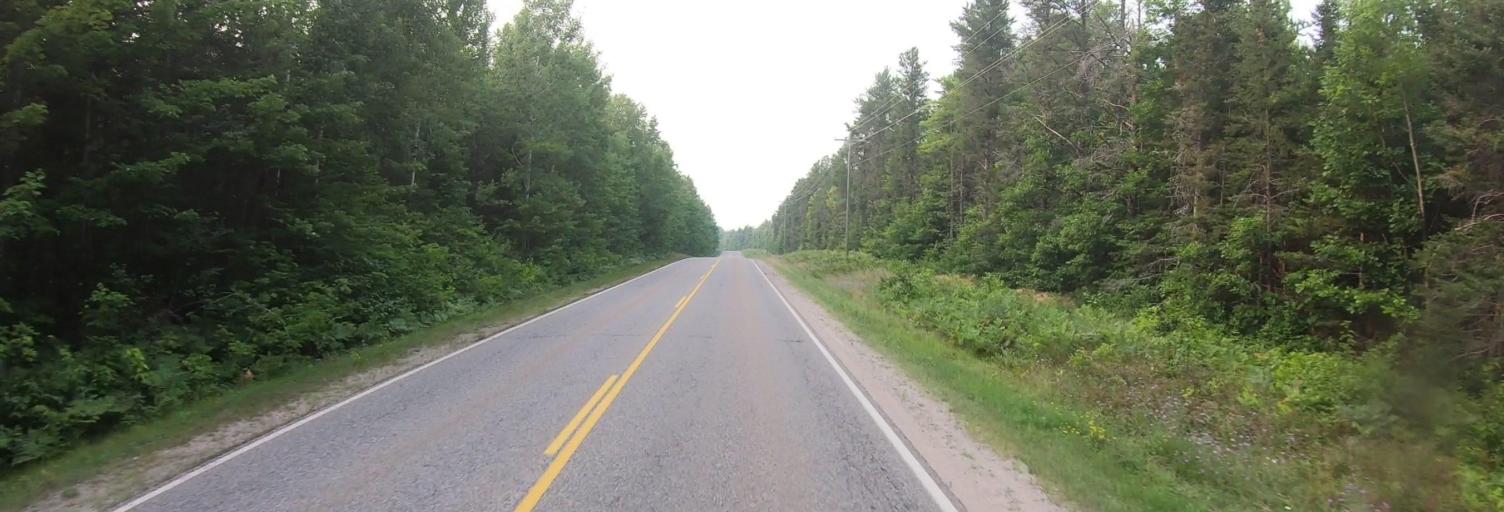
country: US
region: Michigan
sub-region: Chippewa County
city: Sault Ste. Marie
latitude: 46.4736
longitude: -84.6222
